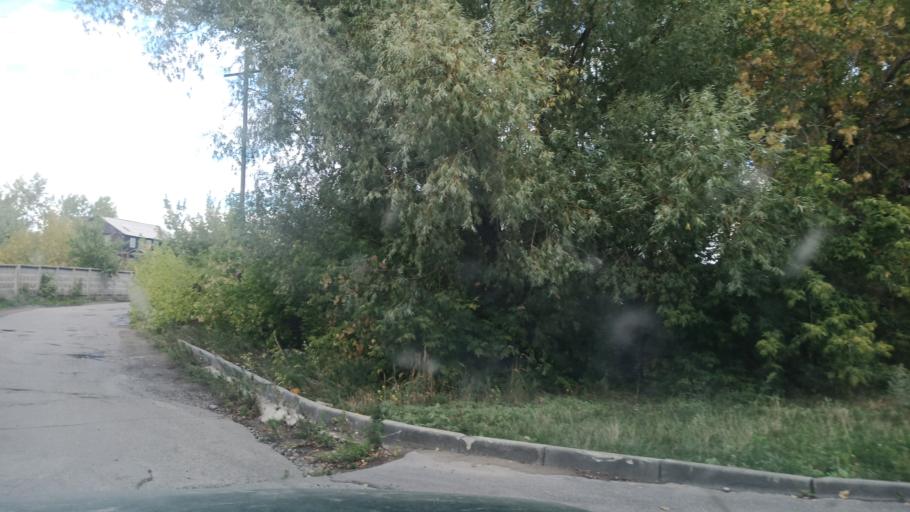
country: RU
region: Altai Krai
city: Zaton
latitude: 53.3316
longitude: 83.8063
